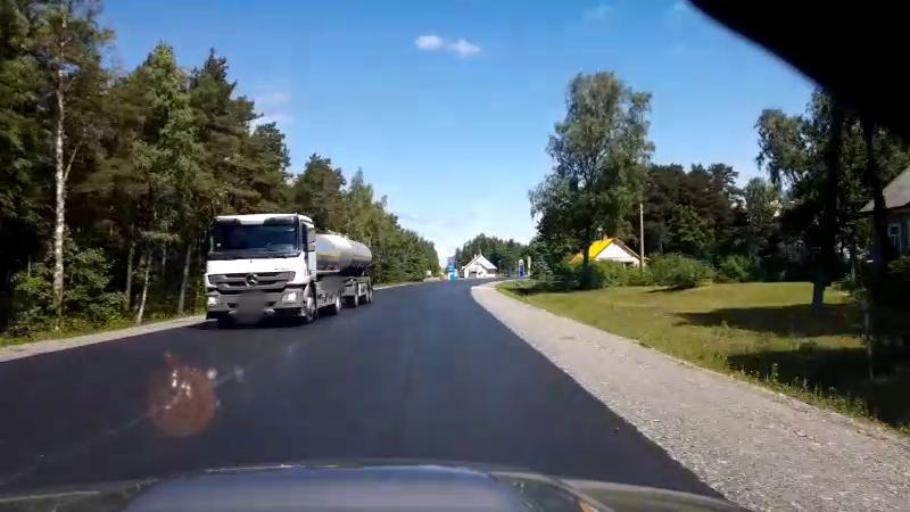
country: LV
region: Salacgrivas
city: Ainazi
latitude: 57.8491
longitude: 24.3534
